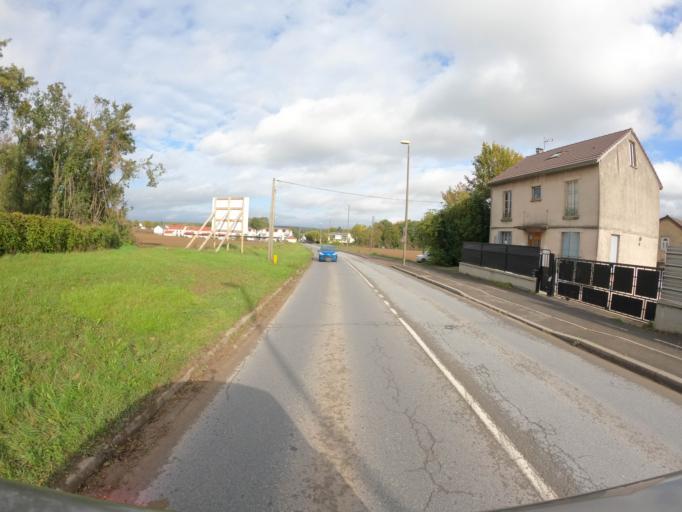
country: FR
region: Ile-de-France
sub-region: Departement de Seine-Saint-Denis
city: Montfermeil
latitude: 48.8952
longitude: 2.5912
